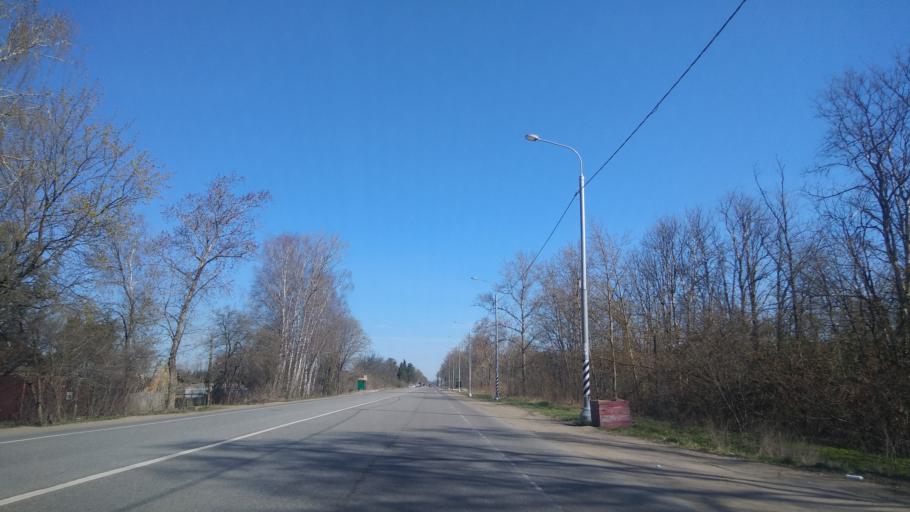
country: RU
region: Moskovskaya
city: Pushkino
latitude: 56.0244
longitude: 37.8713
